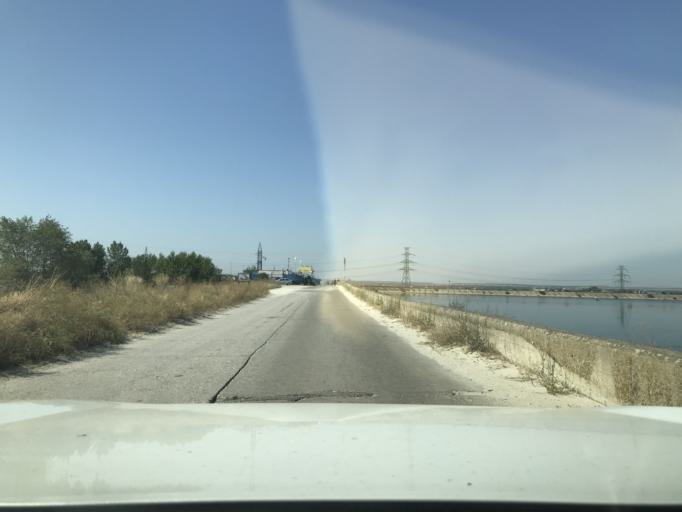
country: RO
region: Olt
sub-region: Comuna Slatioara
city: Slatioara
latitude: 44.3944
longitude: 24.3490
